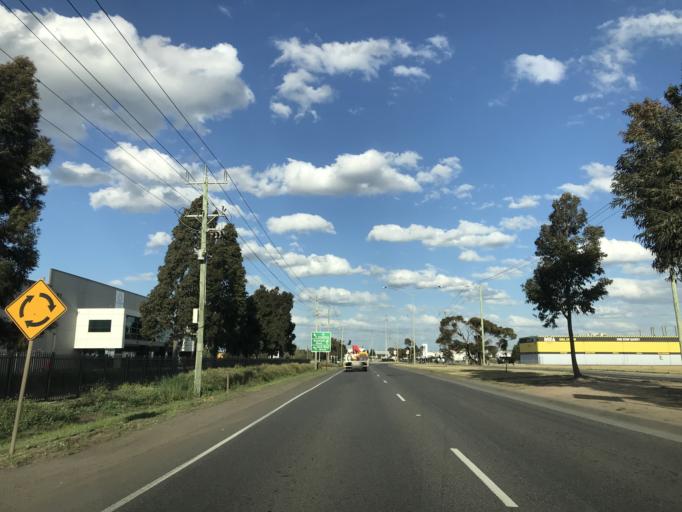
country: AU
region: Victoria
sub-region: Brimbank
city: Sunshine West
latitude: -37.8147
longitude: 144.8014
